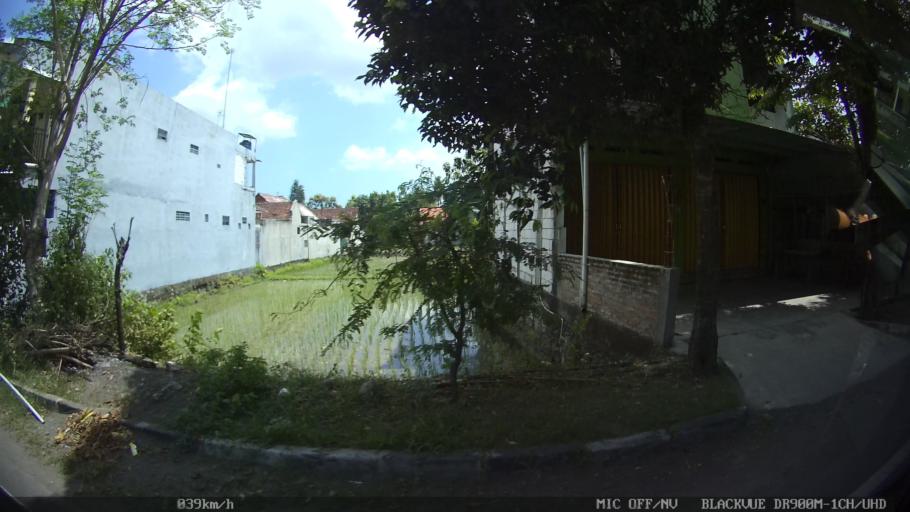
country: ID
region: Daerah Istimewa Yogyakarta
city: Bantul
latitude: -7.8850
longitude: 110.3355
